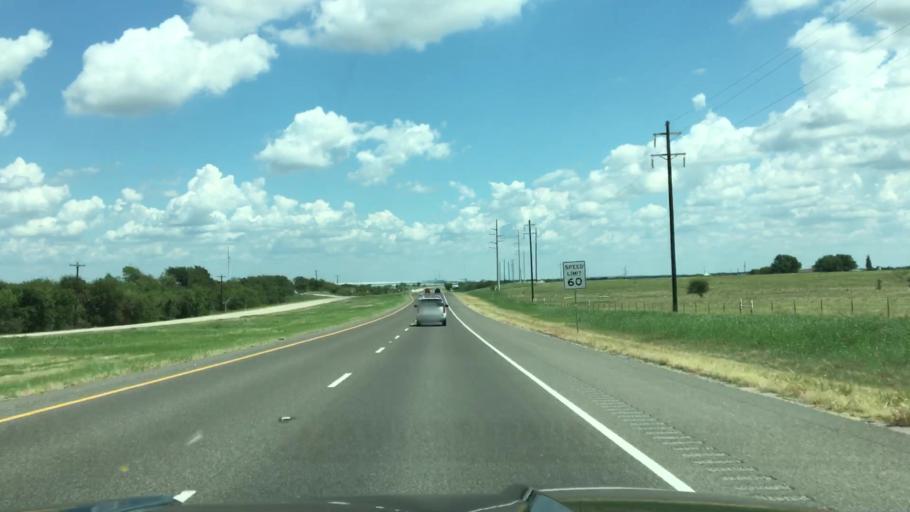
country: US
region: Texas
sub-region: Wise County
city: Rhome
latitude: 33.0366
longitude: -97.4149
